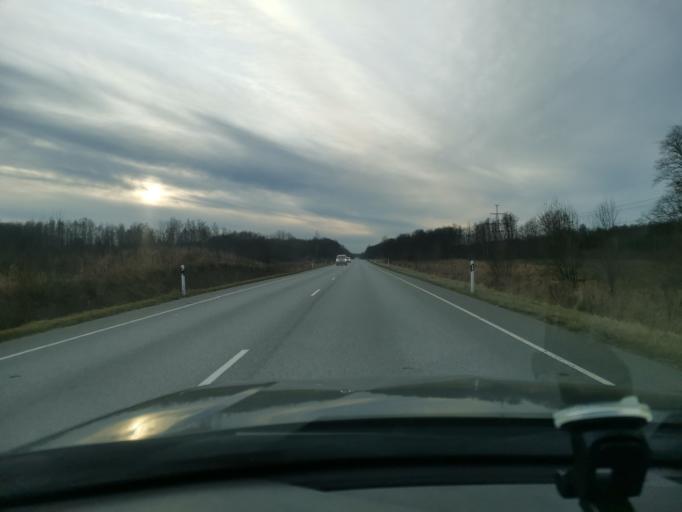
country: EE
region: Ida-Virumaa
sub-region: Narva-Joesuu linn
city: Narva-Joesuu
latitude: 59.3353
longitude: 27.9641
